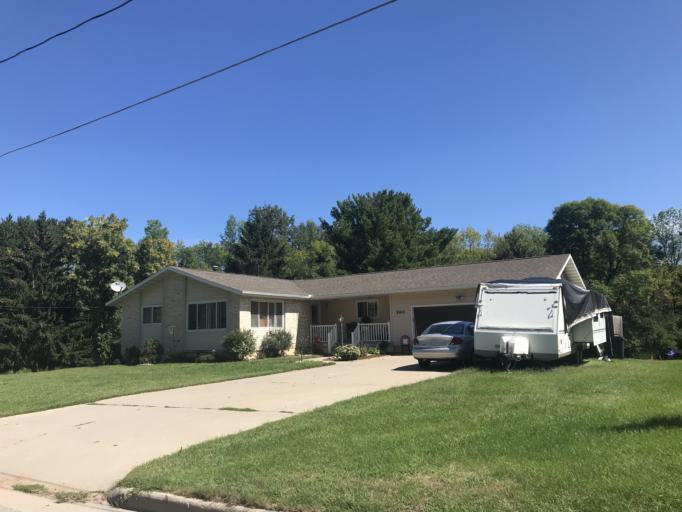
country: US
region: Wisconsin
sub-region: Marinette County
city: Peshtigo
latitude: 45.0583
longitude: -87.7608
